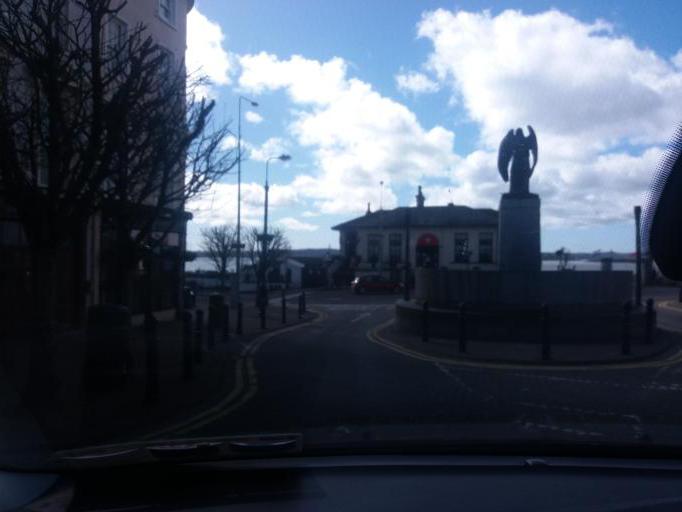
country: IE
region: Munster
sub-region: County Cork
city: Cobh
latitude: 51.8505
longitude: -8.2952
